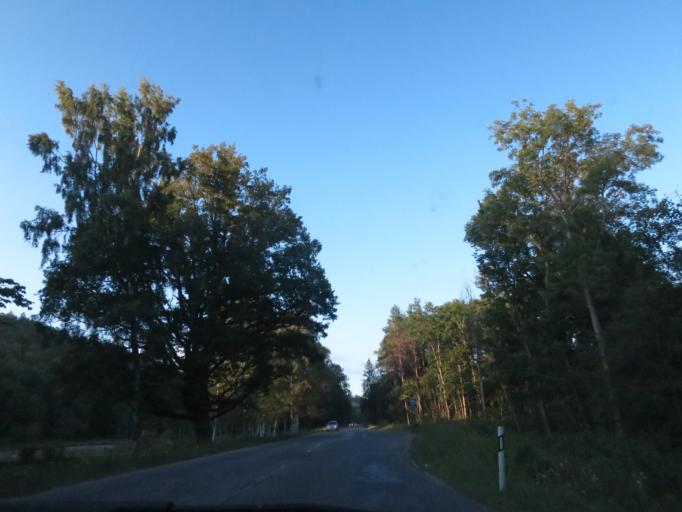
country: LV
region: Sigulda
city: Sigulda
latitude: 57.1712
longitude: 24.8388
